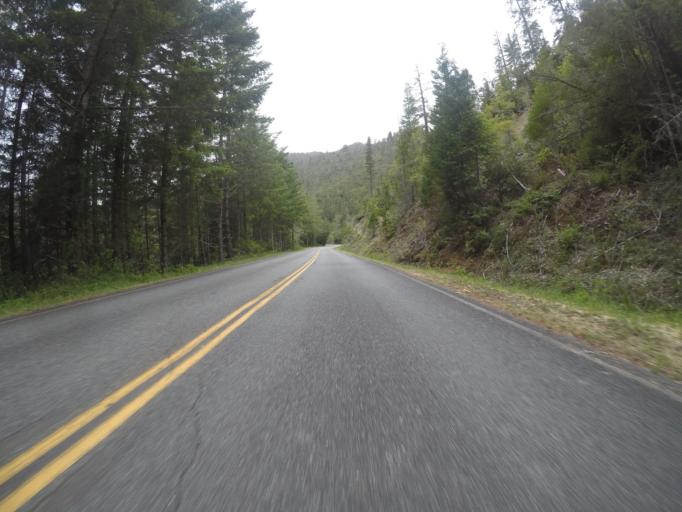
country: US
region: California
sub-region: Del Norte County
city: Bertsch-Oceanview
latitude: 41.7611
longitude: -124.0062
